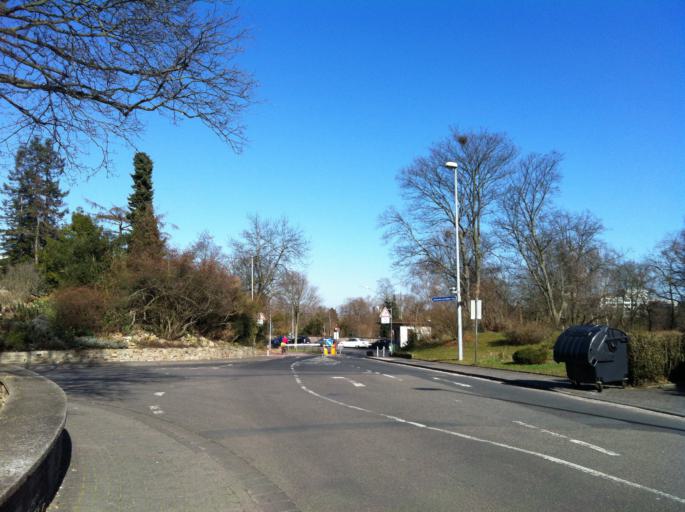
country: DE
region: Rheinland-Pfalz
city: Mainz
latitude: 49.9931
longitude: 8.2454
